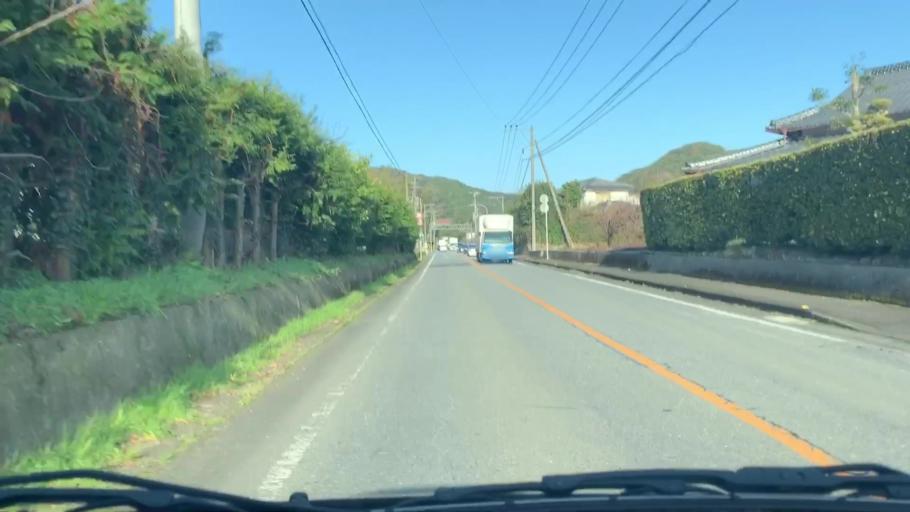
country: JP
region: Saga Prefecture
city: Takeocho-takeo
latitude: 33.2297
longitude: 130.0187
